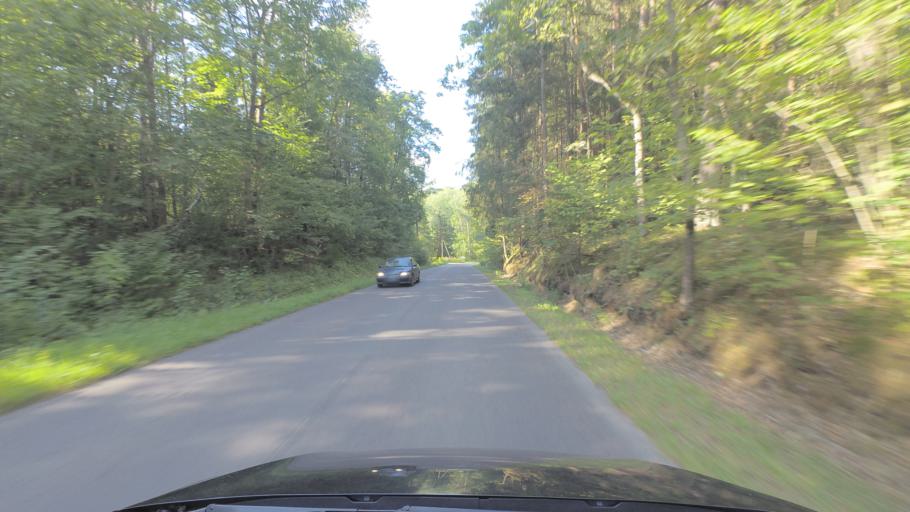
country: LT
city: Nemencine
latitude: 54.8181
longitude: 25.3524
